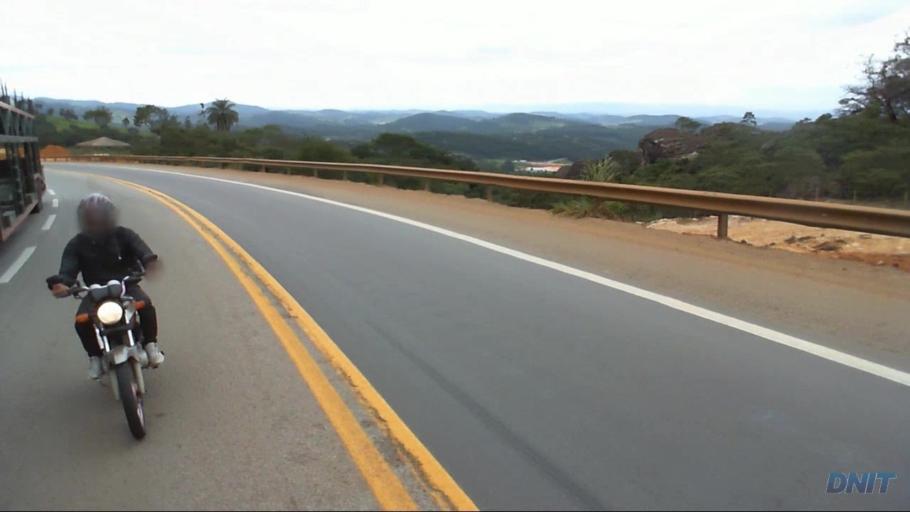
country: BR
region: Minas Gerais
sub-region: Caete
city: Caete
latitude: -19.7476
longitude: -43.5215
